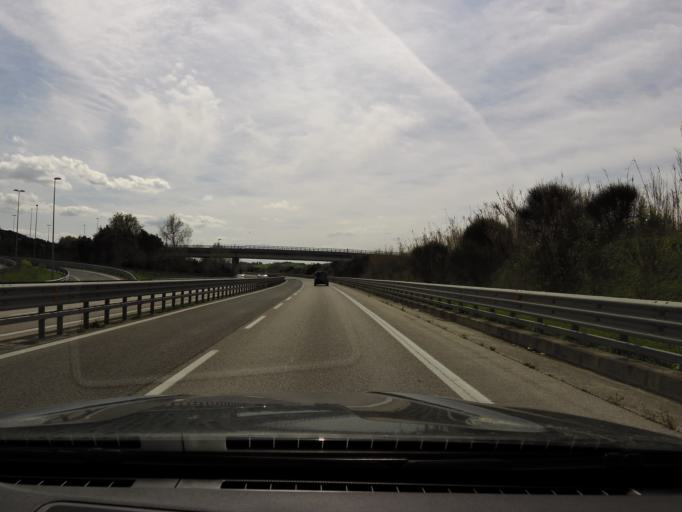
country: IT
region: The Marches
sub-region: Provincia di Ancona
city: San Biagio
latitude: 43.5451
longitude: 13.5148
